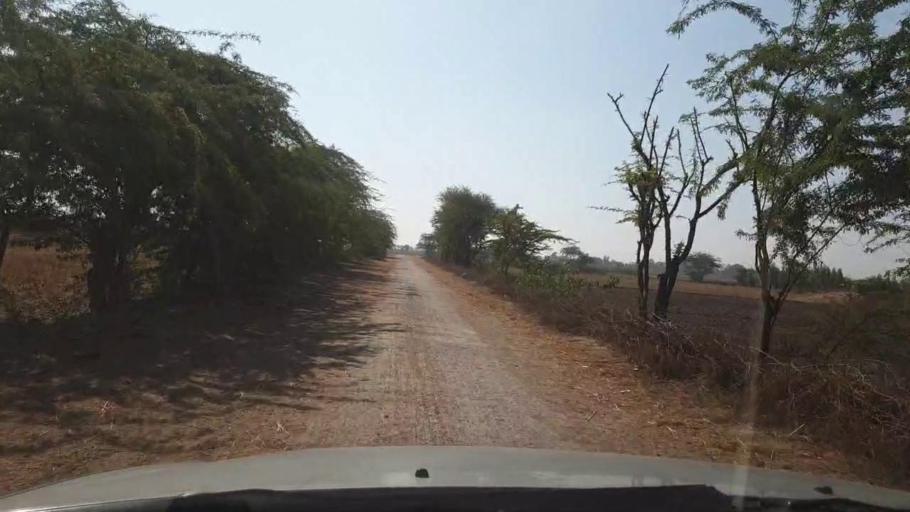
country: PK
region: Sindh
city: Kario
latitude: 24.8944
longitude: 68.5647
